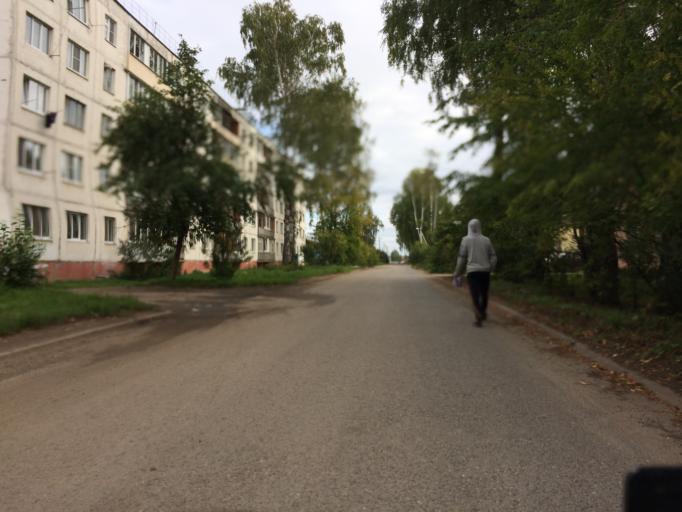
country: RU
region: Mariy-El
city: Yoshkar-Ola
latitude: 56.6571
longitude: 47.9799
